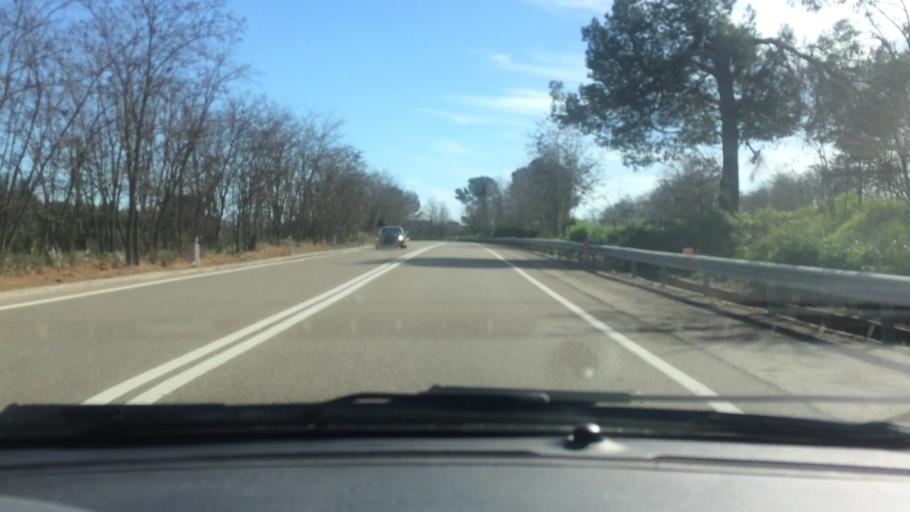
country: IT
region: Basilicate
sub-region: Provincia di Matera
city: Miglionico
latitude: 40.5941
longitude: 16.5594
